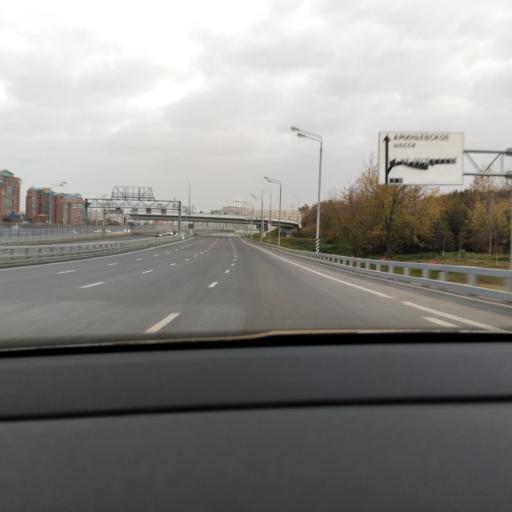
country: RU
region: Moskovskaya
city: Kastanayevo
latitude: 55.7175
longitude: 37.4947
